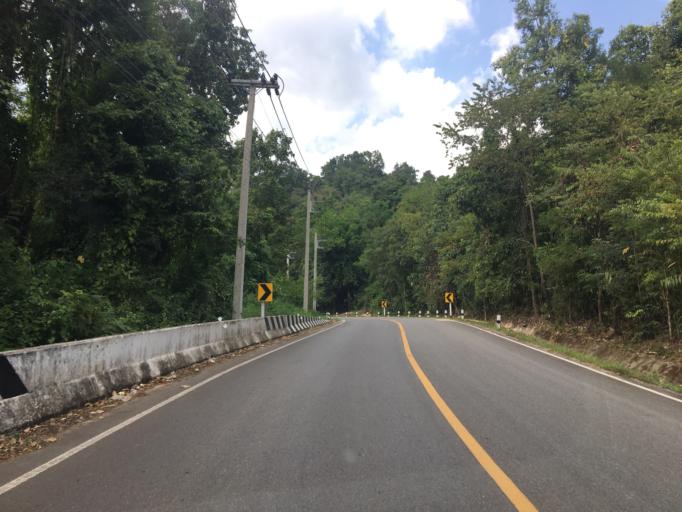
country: TH
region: Nan
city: Nan
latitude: 18.8649
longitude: 100.6321
